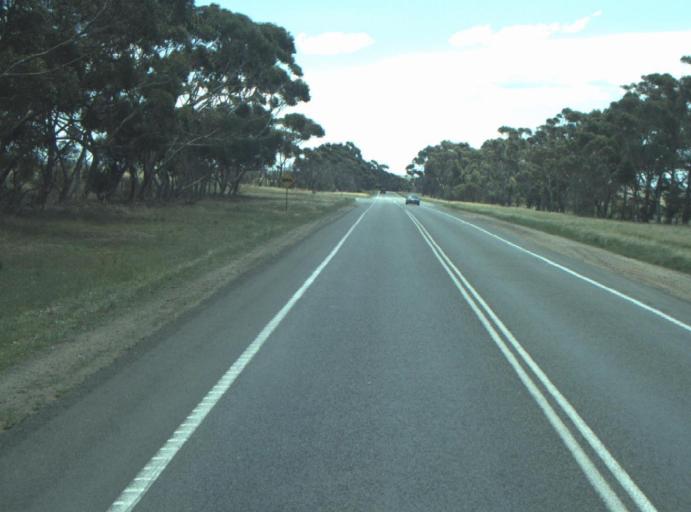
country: AU
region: Victoria
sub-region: Greater Geelong
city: Lara
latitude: -37.9610
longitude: 144.3511
